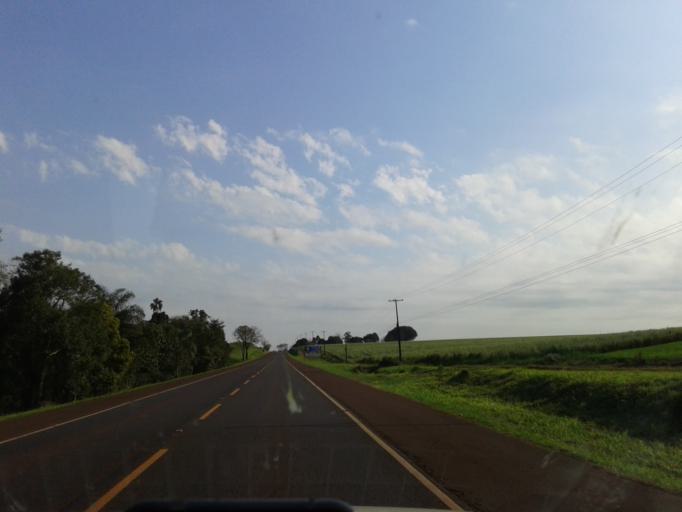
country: PY
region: Itapua
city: Edelira
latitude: -26.7589
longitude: -55.3774
